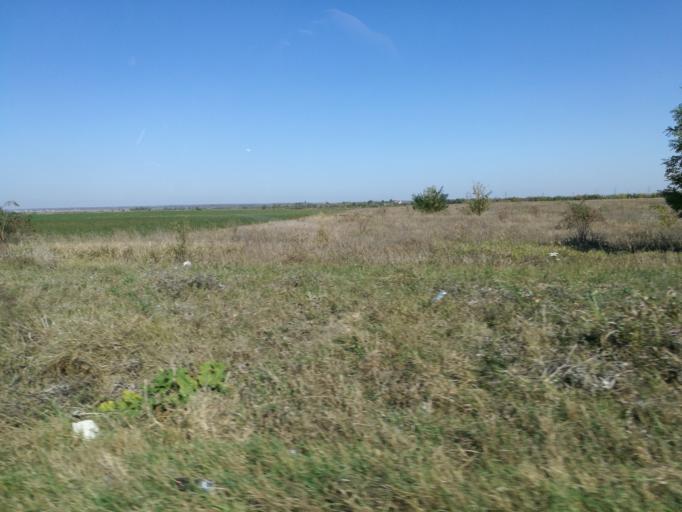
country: RO
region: Giurgiu
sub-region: Comuna Joita
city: Bacu
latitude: 44.4774
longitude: 25.9036
